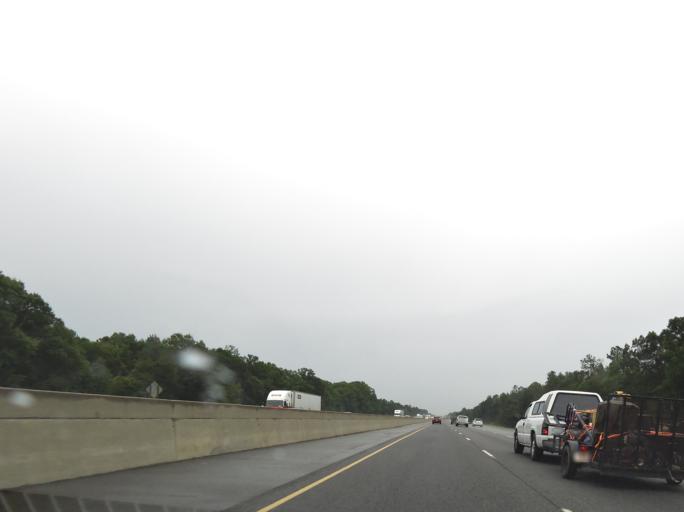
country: US
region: Georgia
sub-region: Turner County
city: Ashburn
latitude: 31.7745
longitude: -83.6815
